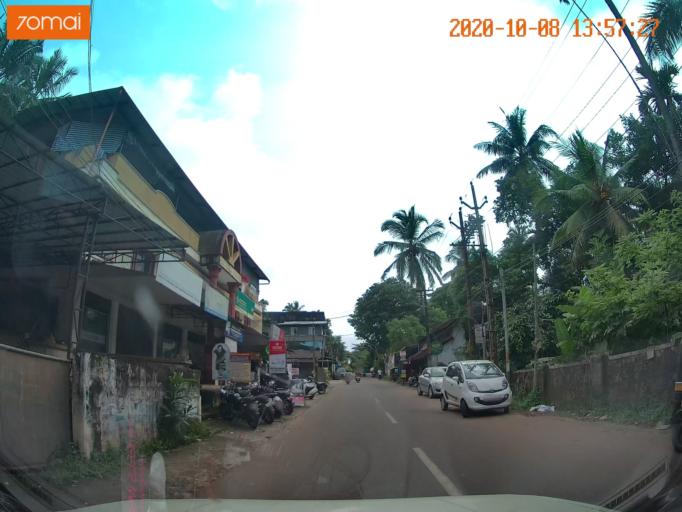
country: IN
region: Kerala
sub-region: Kozhikode
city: Kozhikode
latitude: 11.2881
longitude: 75.8015
